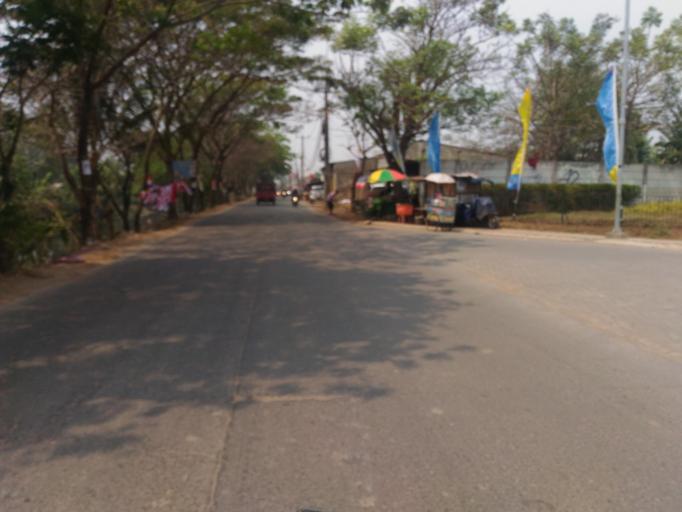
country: ID
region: West Java
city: Pasarkemis
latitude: -6.1388
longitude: 106.5424
